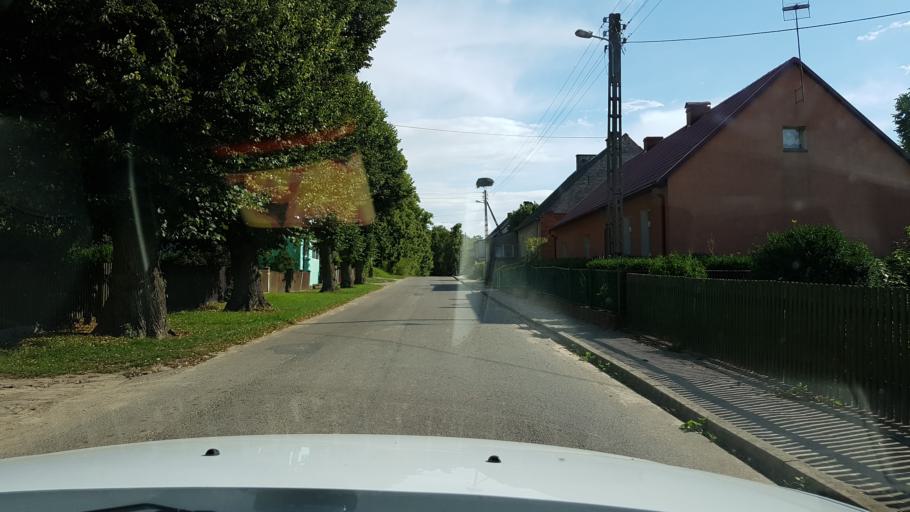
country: PL
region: West Pomeranian Voivodeship
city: Trzcinsko Zdroj
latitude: 52.9501
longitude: 14.5490
